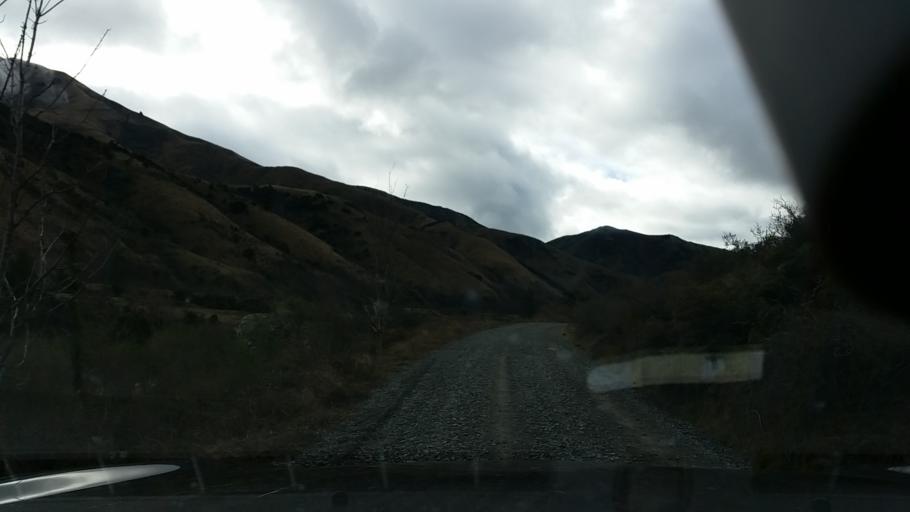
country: NZ
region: Tasman
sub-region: Tasman District
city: Brightwater
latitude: -41.7478
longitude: 173.4103
